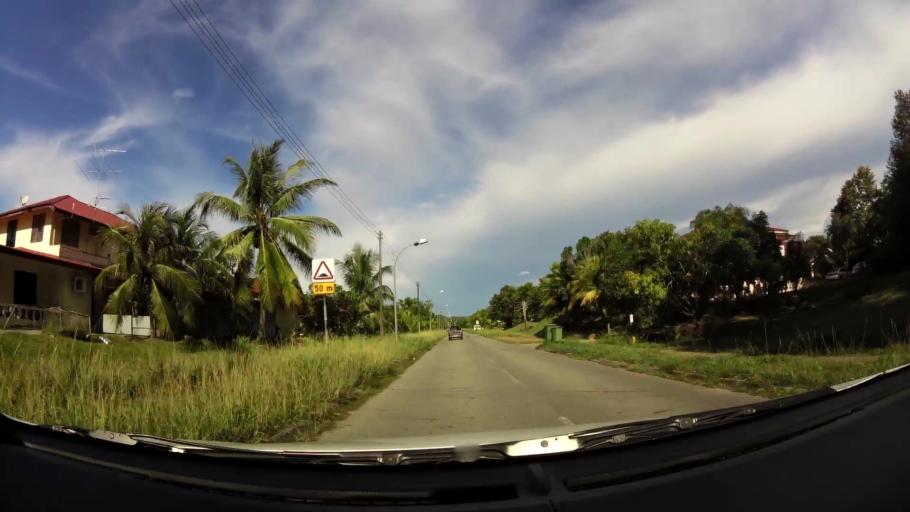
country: BN
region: Brunei and Muara
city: Bandar Seri Begawan
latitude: 4.9707
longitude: 114.9578
